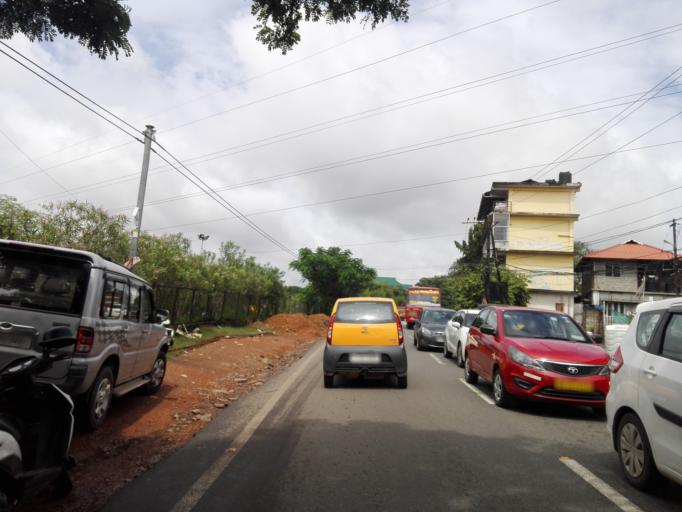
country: IN
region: Kerala
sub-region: Ernakulam
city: Elur
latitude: 10.0179
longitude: 76.3492
